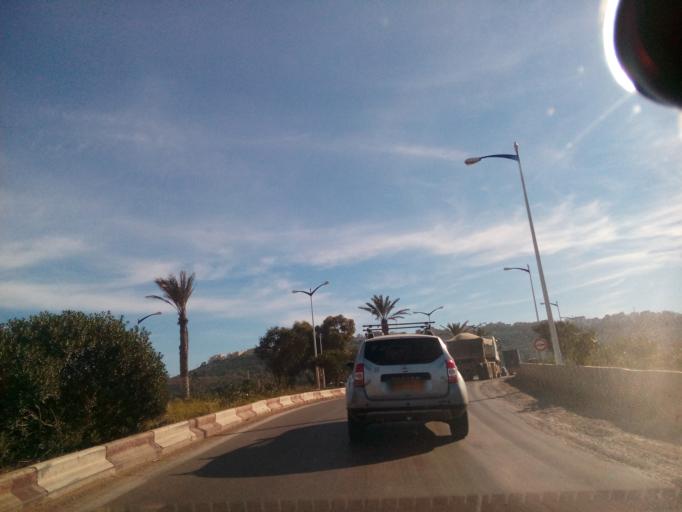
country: DZ
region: Mostaganem
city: Mostaganem
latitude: 35.9108
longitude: 0.0771
